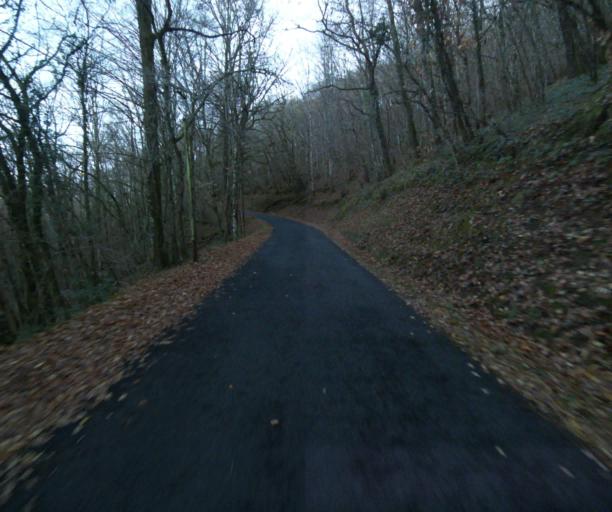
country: FR
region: Limousin
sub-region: Departement de la Correze
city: Laguenne
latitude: 45.2362
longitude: 1.7992
